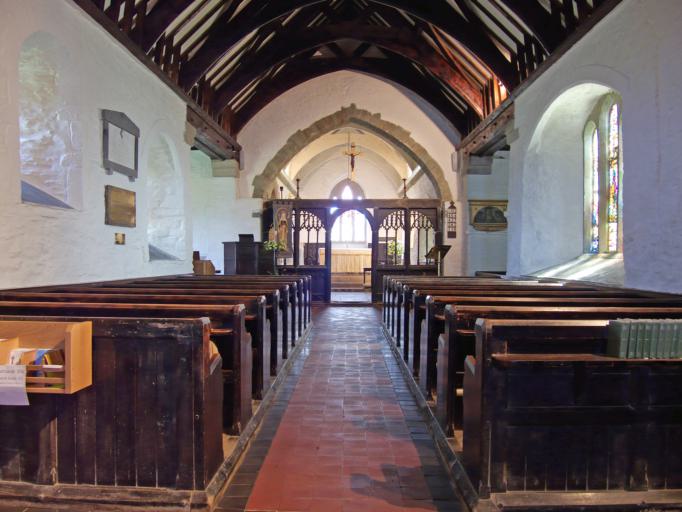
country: GB
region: England
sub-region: Cornwall
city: Tintagel
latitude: 50.6630
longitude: -4.7598
